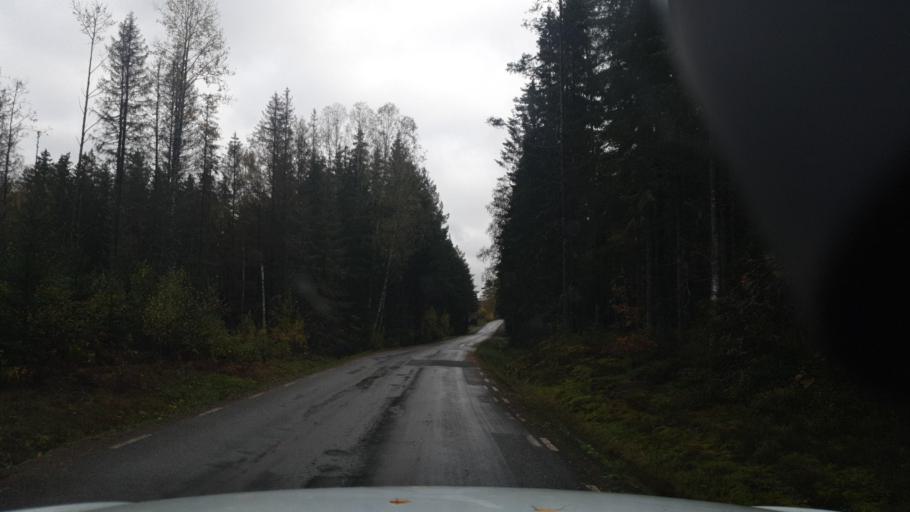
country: SE
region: Vaermland
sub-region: Karlstads Kommun
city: Valberg
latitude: 59.4228
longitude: 13.0945
